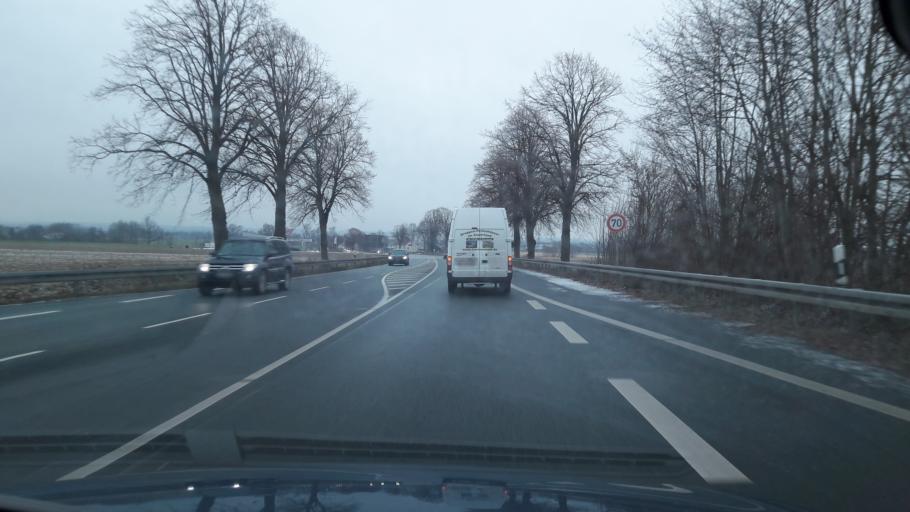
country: DE
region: North Rhine-Westphalia
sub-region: Regierungsbezirk Arnsberg
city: Lippstadt
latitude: 51.6483
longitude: 8.3433
